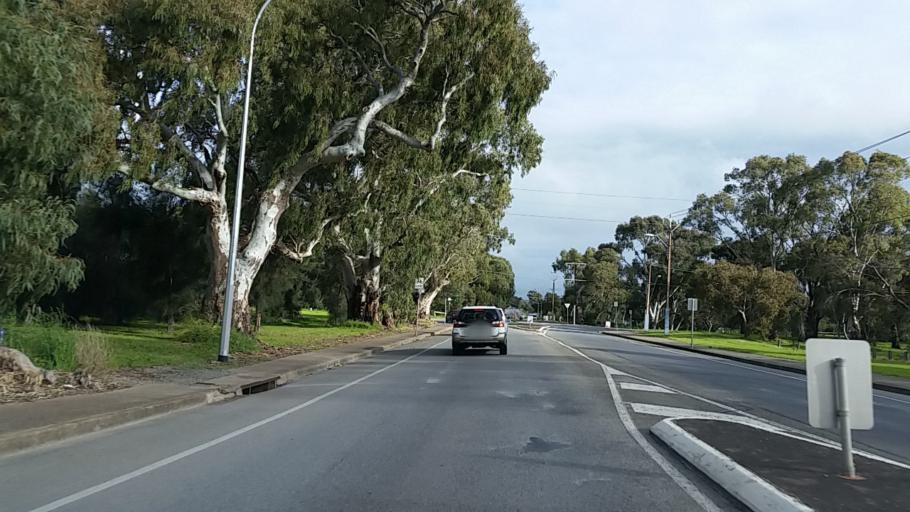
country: AU
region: South Australia
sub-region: Onkaparinga
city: Morphett Vale
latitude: -35.1352
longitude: 138.5371
